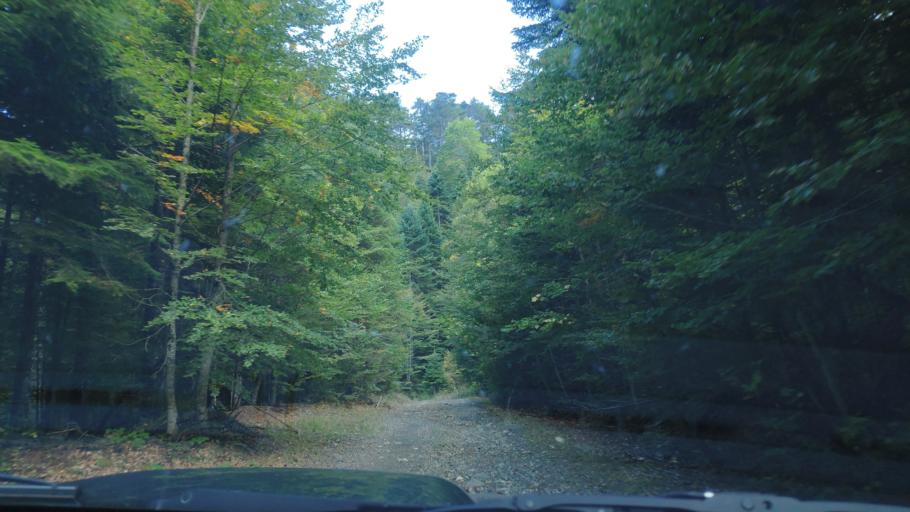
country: AL
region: Korce
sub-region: Rrethi i Devollit
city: Miras
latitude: 40.3376
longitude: 20.8964
